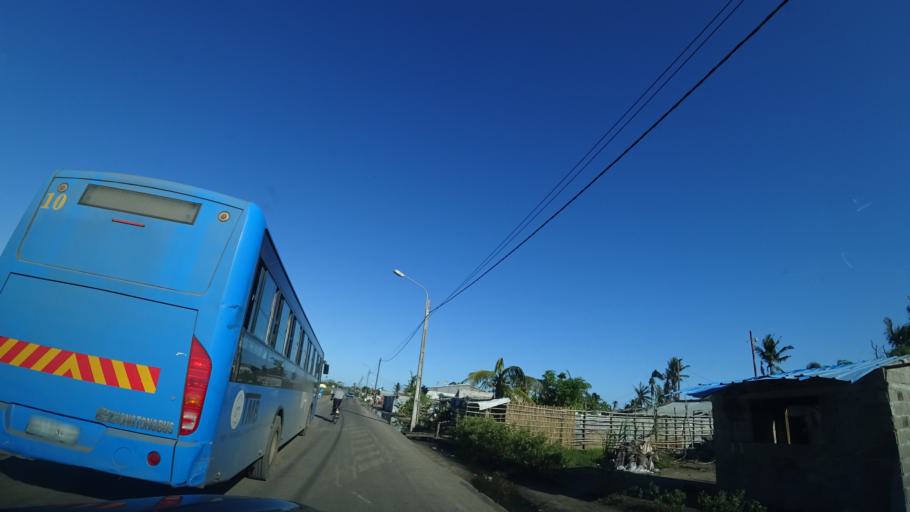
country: MZ
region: Sofala
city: Beira
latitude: -19.7915
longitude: 34.8878
